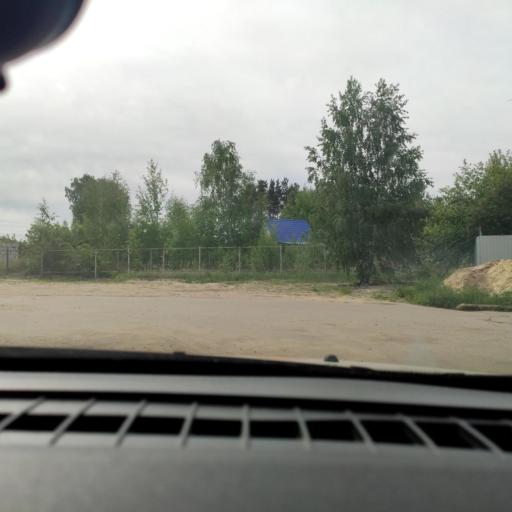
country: RU
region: Voronezj
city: Podgornoye
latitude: 51.8402
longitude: 39.1871
